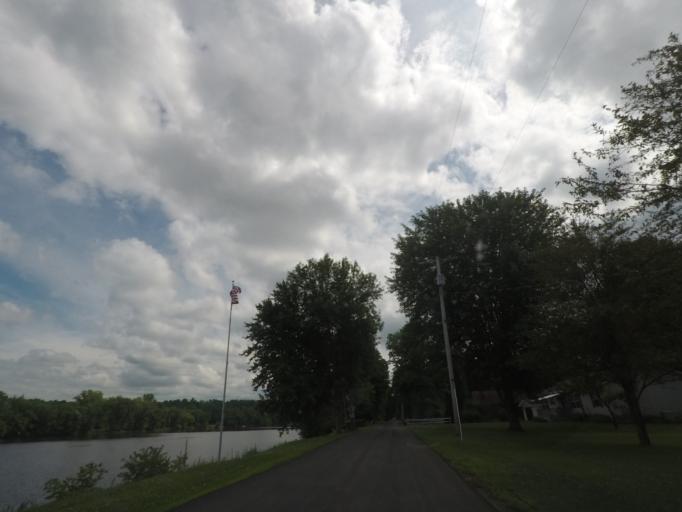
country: US
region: New York
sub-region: Saratoga County
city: Stillwater
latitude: 42.9893
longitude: -73.6096
